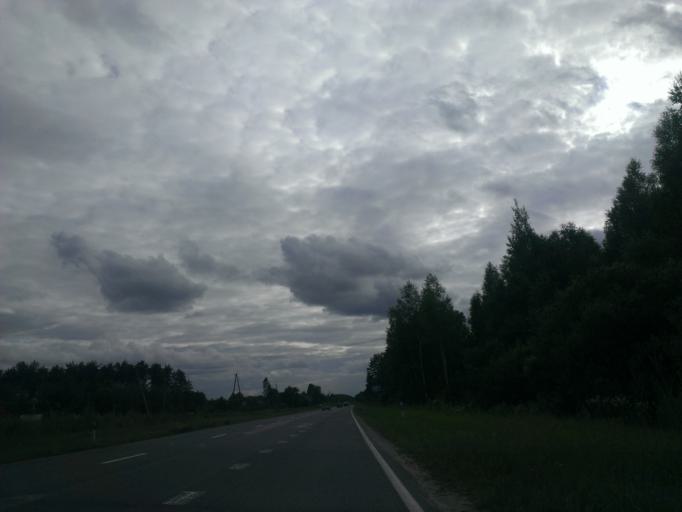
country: LV
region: Incukalns
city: Vangazi
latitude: 57.0926
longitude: 24.5612
